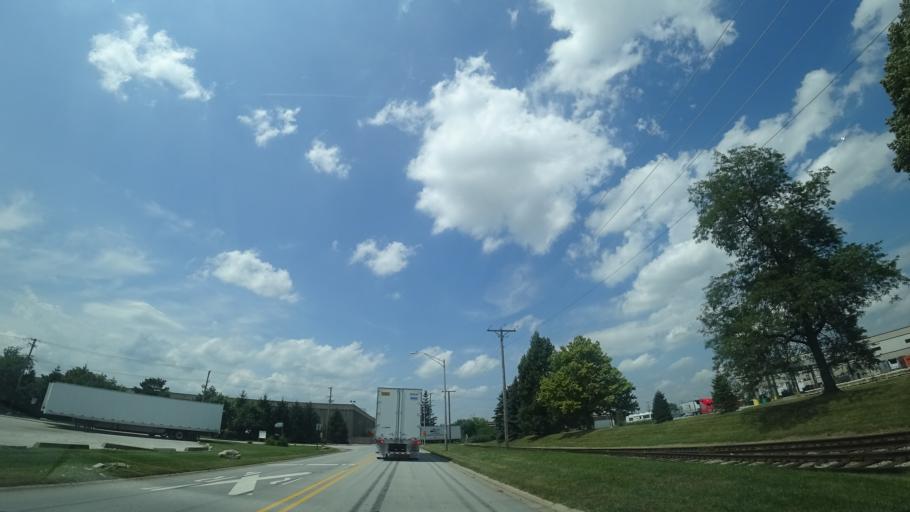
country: US
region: Illinois
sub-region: Cook County
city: Crestwood
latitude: 41.6719
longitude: -87.7577
